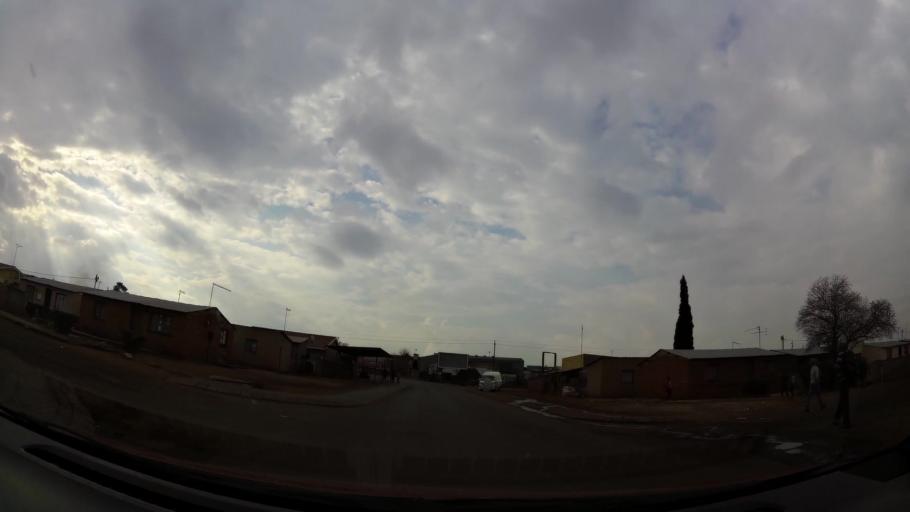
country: ZA
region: Gauteng
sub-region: Sedibeng District Municipality
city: Vanderbijlpark
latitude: -26.6633
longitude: 27.8513
